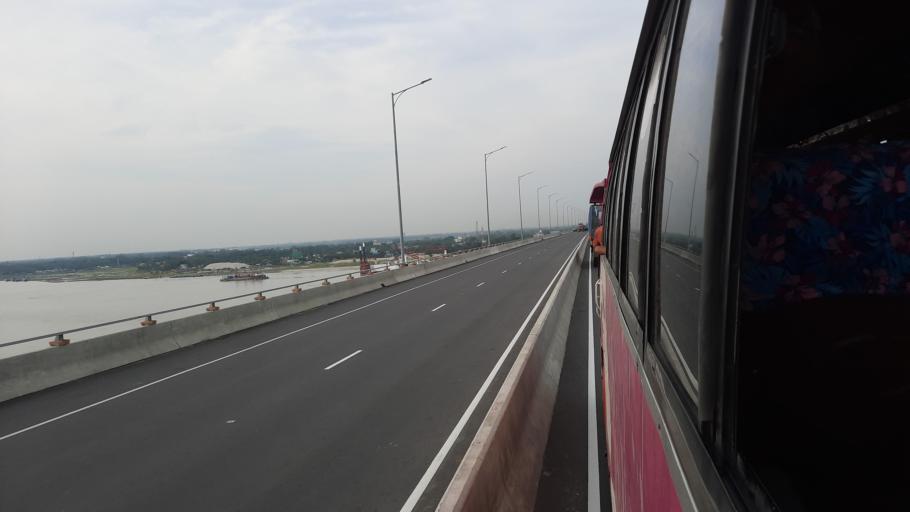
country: BD
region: Dhaka
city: Char Bhadrasan
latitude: 23.4636
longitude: 90.2631
